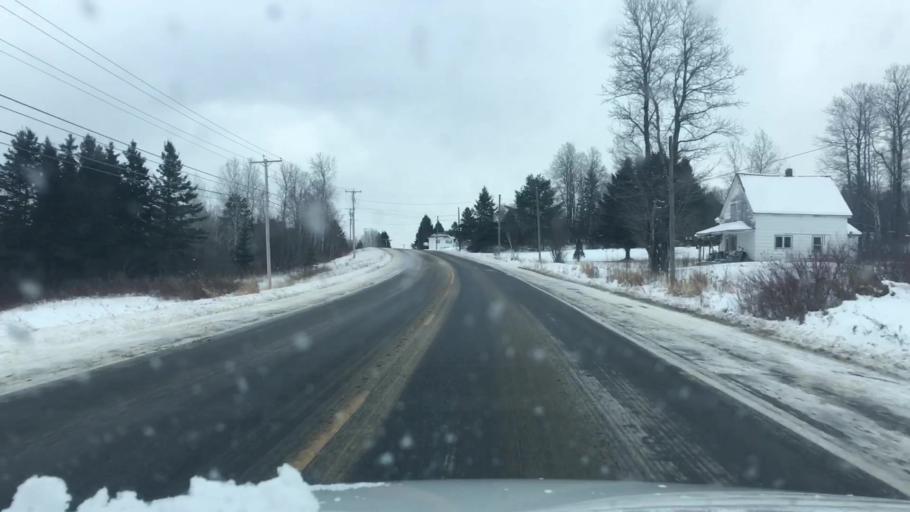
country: US
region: Maine
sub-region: Aroostook County
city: Madawaska
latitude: 47.3196
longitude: -68.1682
